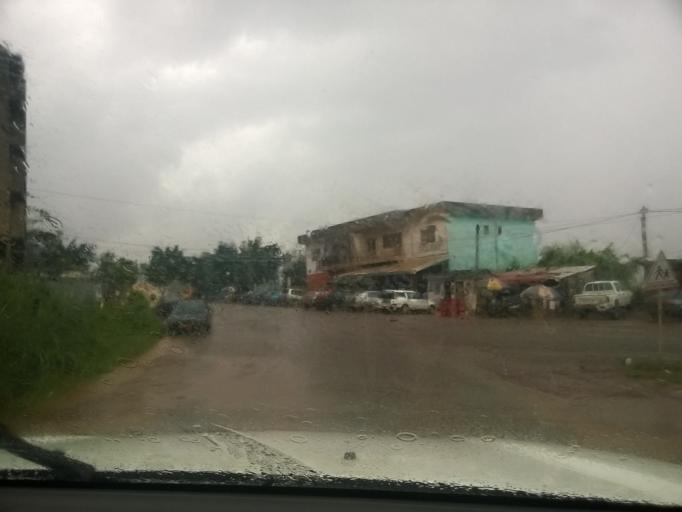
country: CM
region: Centre
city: Yaounde
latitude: 3.8721
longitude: 11.5337
